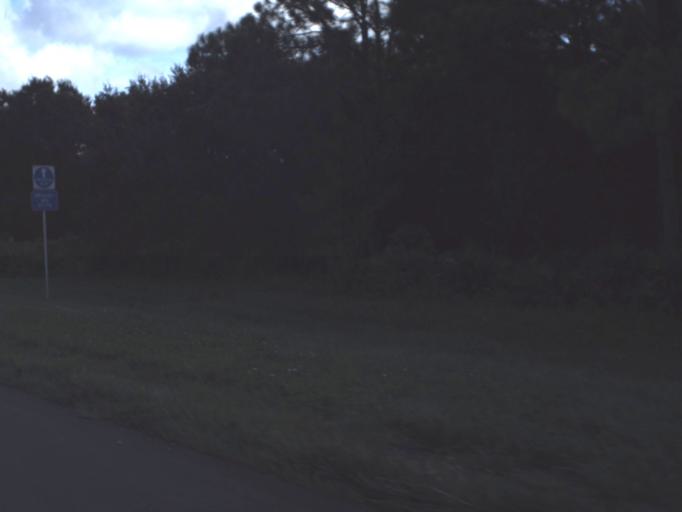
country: US
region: Florida
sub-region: Sarasota County
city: The Meadows
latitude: 27.3632
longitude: -82.4459
